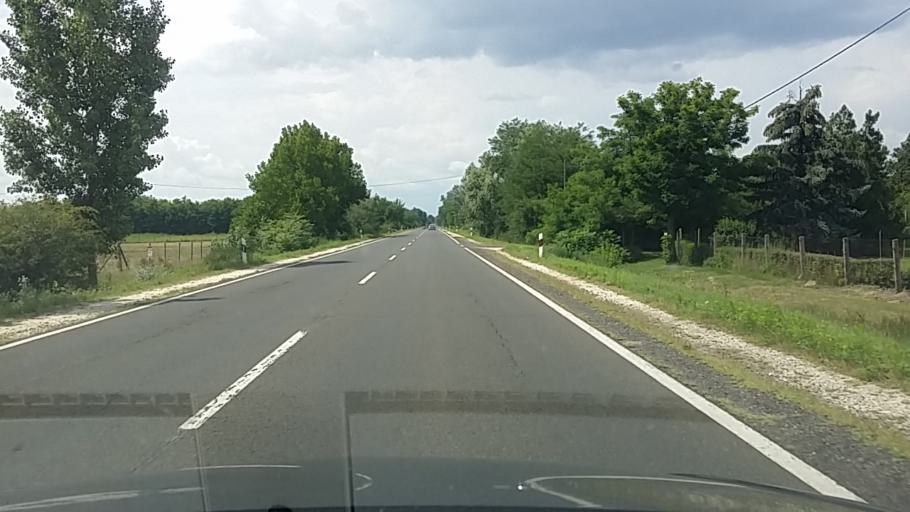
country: HU
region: Pest
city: Taborfalva
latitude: 47.0714
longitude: 19.4961
